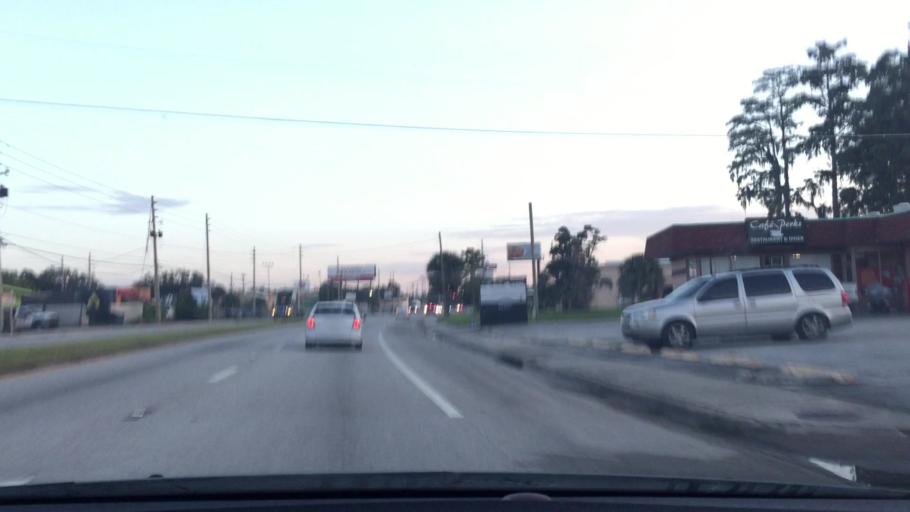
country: US
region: Florida
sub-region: Orange County
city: Fairview Shores
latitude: 28.5751
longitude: -81.4068
